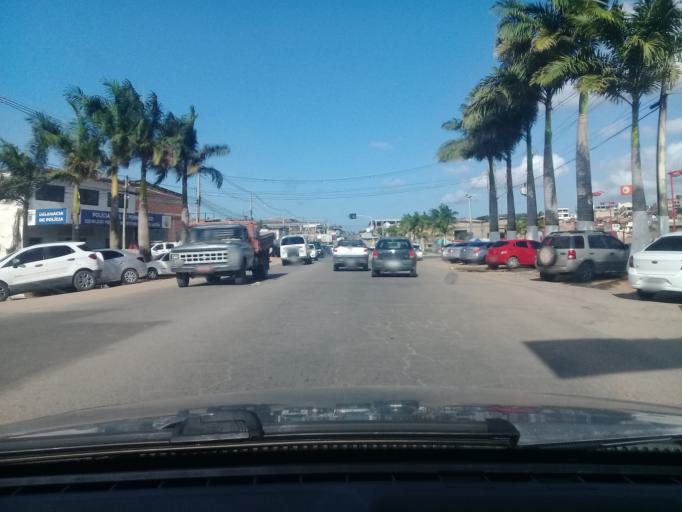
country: BR
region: Pernambuco
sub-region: Vitoria De Santo Antao
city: Vitoria de Santo Antao
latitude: -8.1142
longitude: -35.2828
